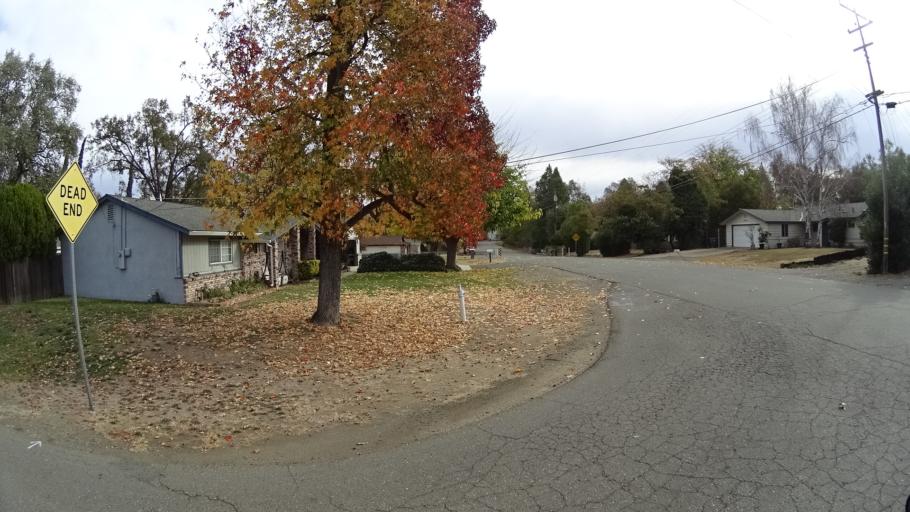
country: US
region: California
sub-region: Sacramento County
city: Citrus Heights
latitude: 38.7066
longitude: -121.2464
